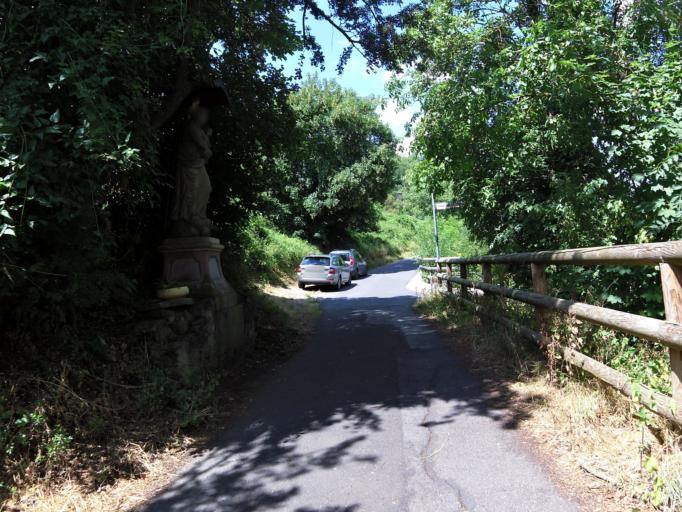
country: DE
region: Bavaria
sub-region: Regierungsbezirk Unterfranken
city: Wuerzburg
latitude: 49.7787
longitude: 9.9232
